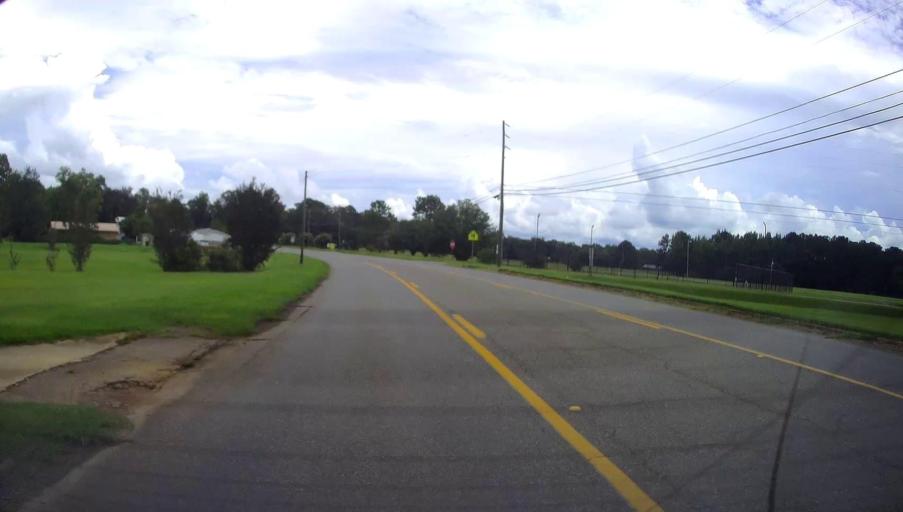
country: US
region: Georgia
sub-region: Schley County
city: Ellaville
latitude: 32.2394
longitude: -84.3152
